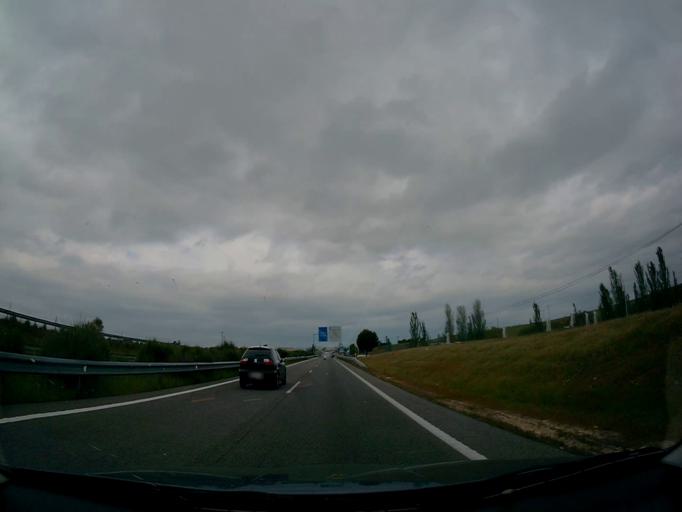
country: ES
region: Madrid
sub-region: Provincia de Madrid
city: Brunete
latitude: 40.3886
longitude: -3.9827
